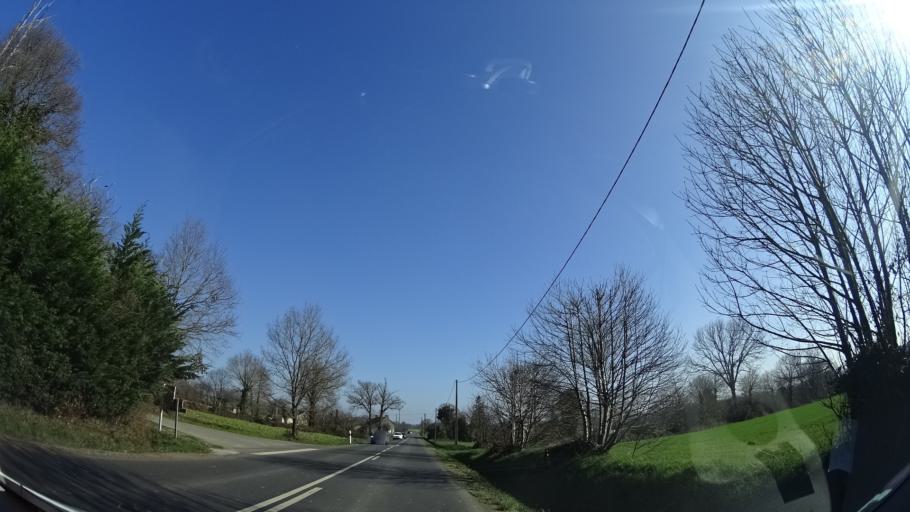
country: FR
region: Brittany
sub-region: Departement d'Ille-et-Vilaine
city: Meillac
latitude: 48.4080
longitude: -1.7834
